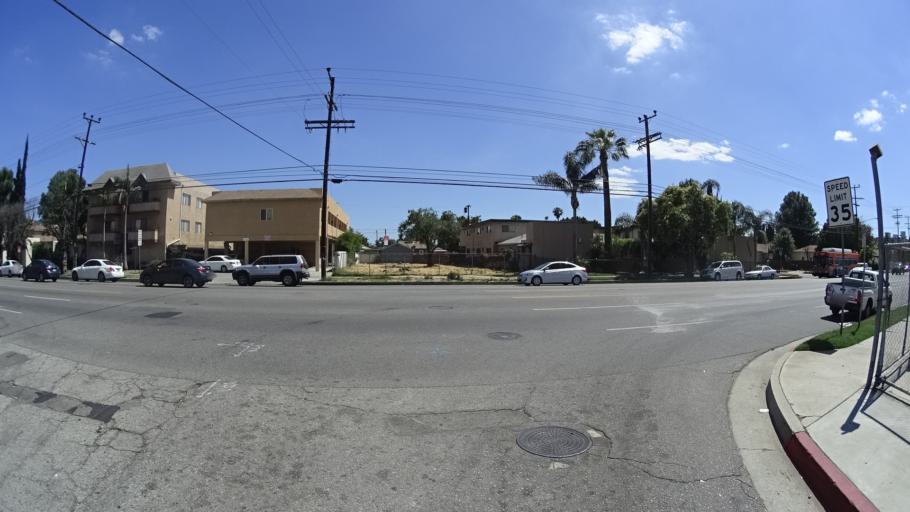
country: US
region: California
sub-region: Los Angeles County
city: Van Nuys
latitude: 34.2217
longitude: -118.4631
